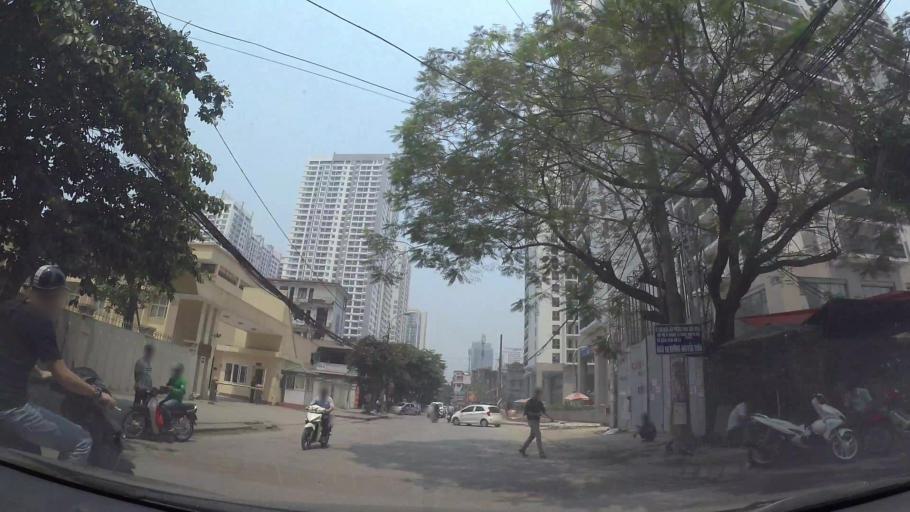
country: VN
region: Ha Noi
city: Thanh Xuan
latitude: 20.9963
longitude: 105.8050
